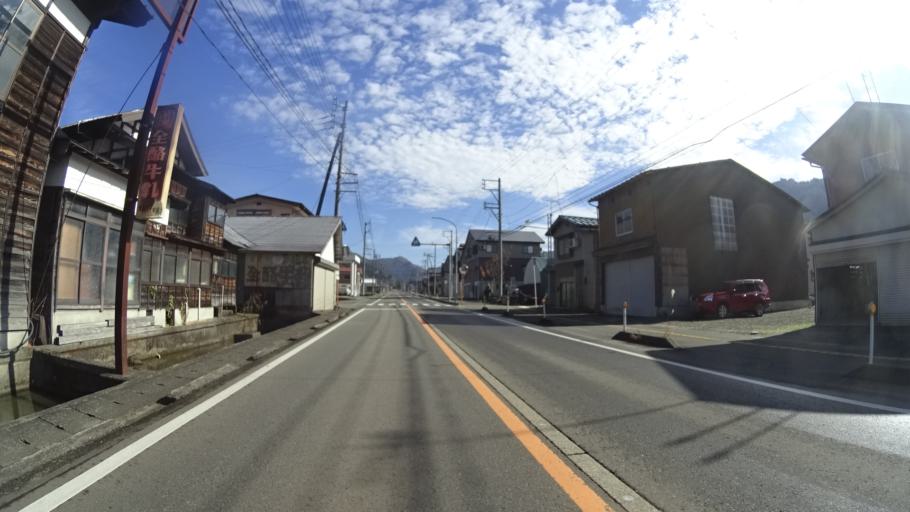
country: JP
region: Niigata
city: Muikamachi
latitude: 37.2271
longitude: 139.0000
